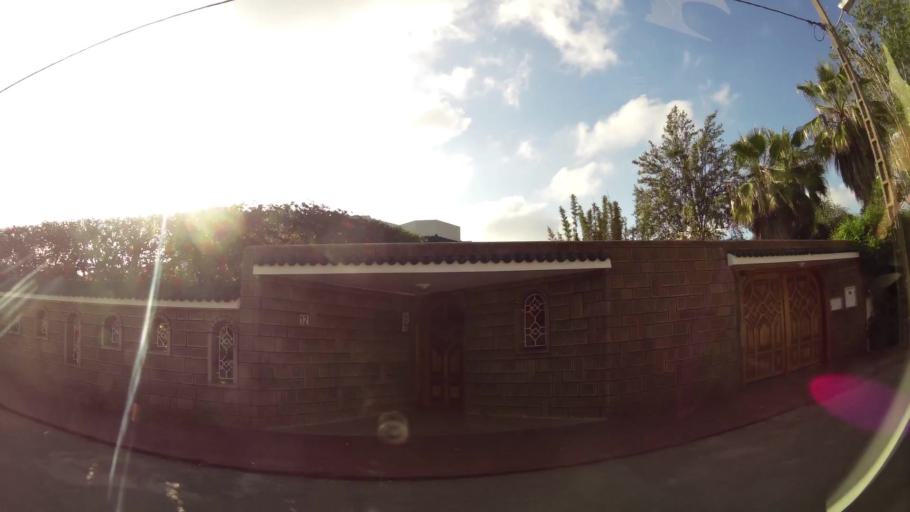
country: MA
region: Rabat-Sale-Zemmour-Zaer
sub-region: Rabat
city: Rabat
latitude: 33.9605
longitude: -6.8546
